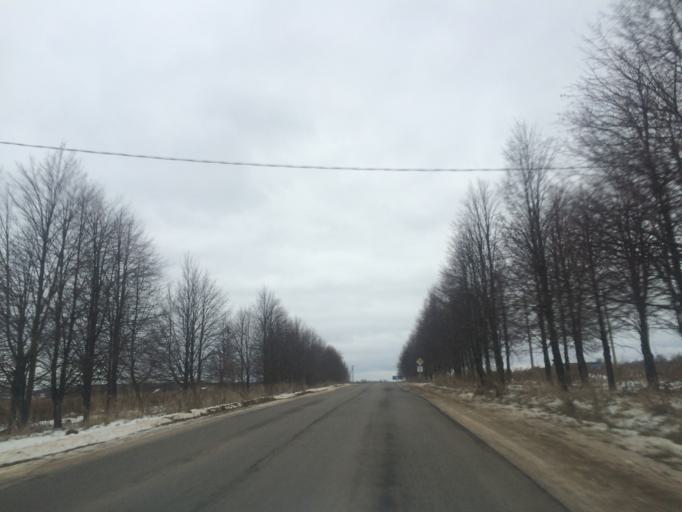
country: RU
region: Tula
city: Kosaya Gora
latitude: 54.1582
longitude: 37.4342
